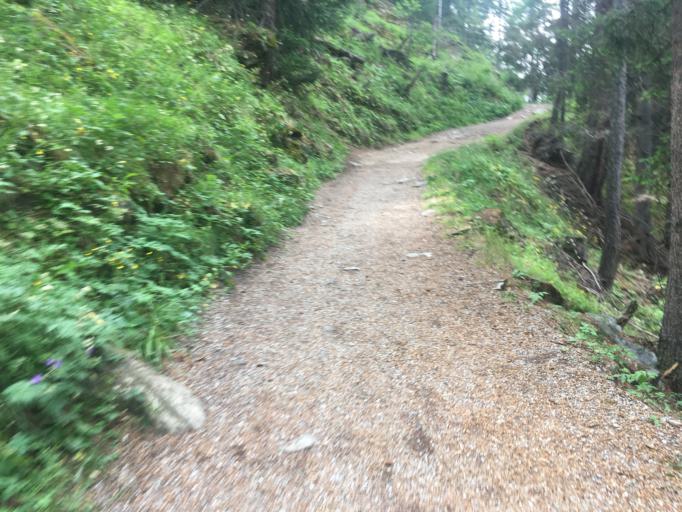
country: CH
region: Valais
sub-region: Visp District
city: Zermatt
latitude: 46.0128
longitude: 7.7510
